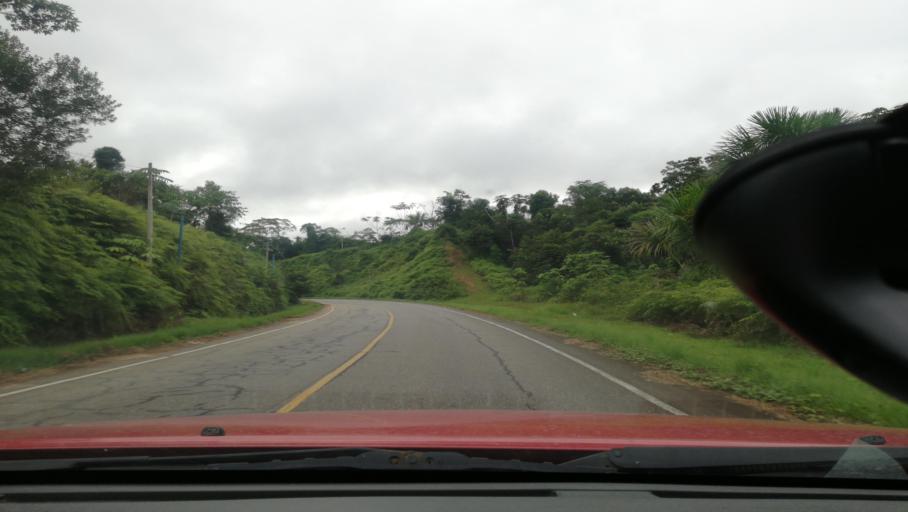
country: PE
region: Loreto
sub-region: Provincia de Loreto
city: Nauta
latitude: -4.4522
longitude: -73.5916
